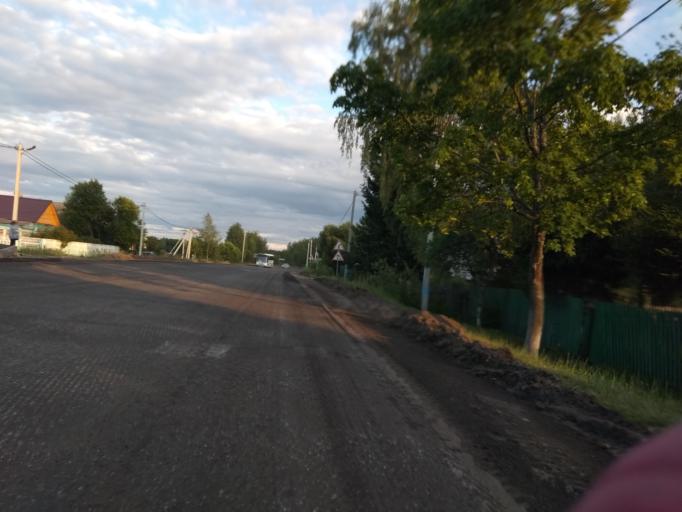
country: RU
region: Moskovskaya
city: Misheronskiy
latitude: 55.6494
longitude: 39.7561
